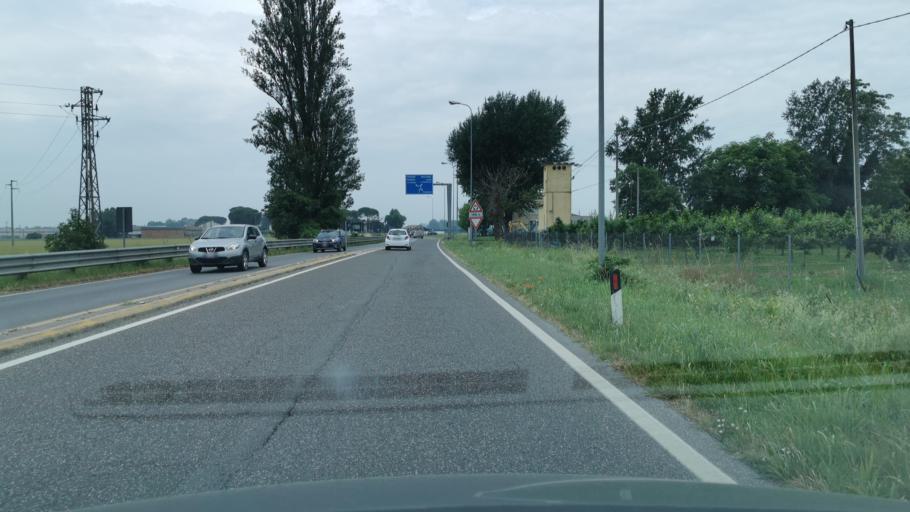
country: IT
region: Emilia-Romagna
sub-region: Provincia di Ravenna
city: Godo
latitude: 44.3906
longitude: 12.0539
